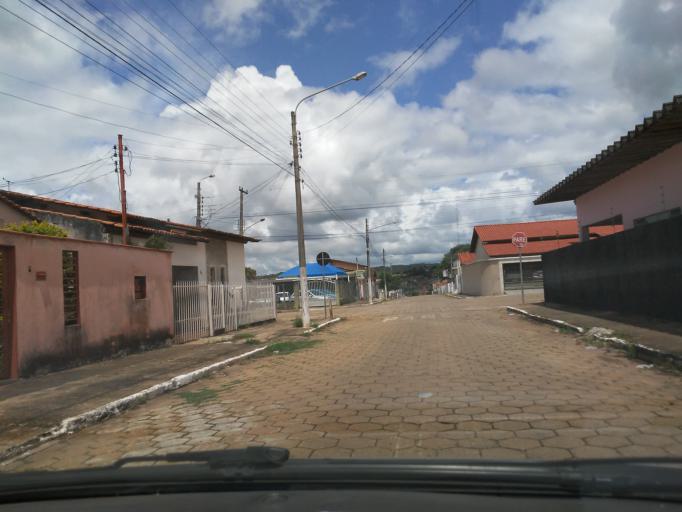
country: BR
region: Goias
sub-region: Ipameri
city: Ipameri
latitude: -17.7294
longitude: -48.1628
